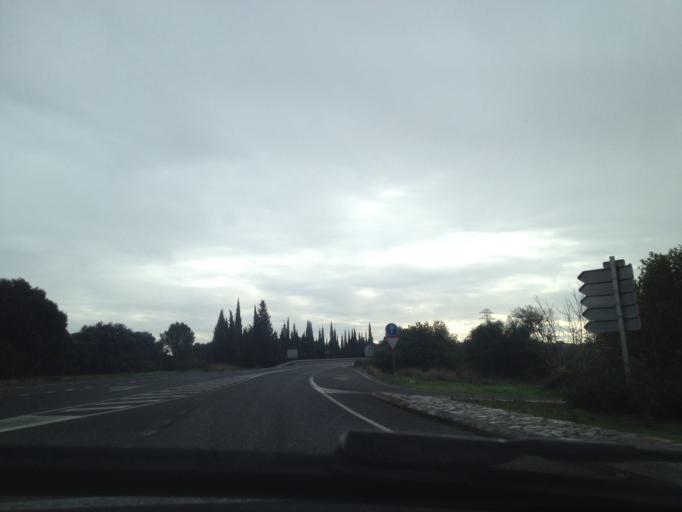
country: ES
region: Balearic Islands
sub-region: Illes Balears
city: Sineu
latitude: 39.6525
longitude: 3.0117
